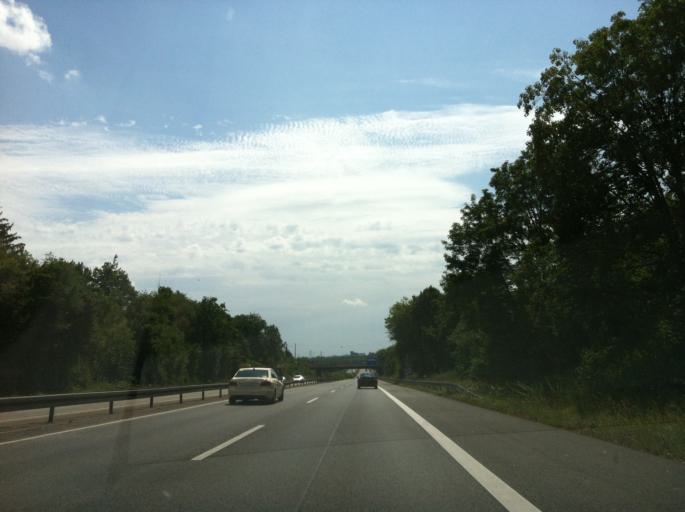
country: DE
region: Hesse
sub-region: Regierungsbezirk Darmstadt
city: Eschborn
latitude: 50.1268
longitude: 8.5768
